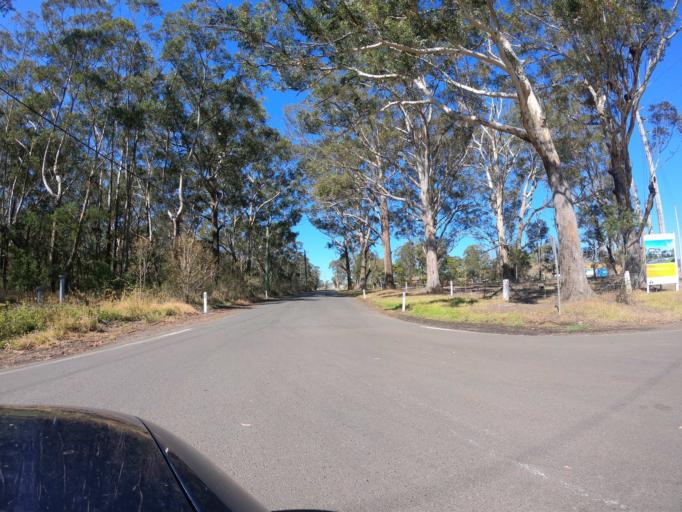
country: AU
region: New South Wales
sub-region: Wollongong
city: Dapto
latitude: -34.4745
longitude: 150.7905
